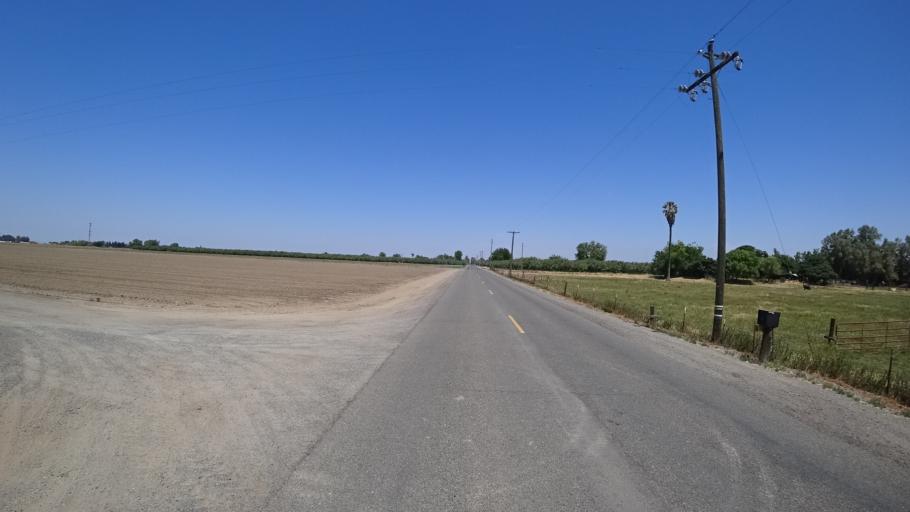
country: US
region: California
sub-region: Kings County
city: Lemoore
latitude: 36.2608
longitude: -119.7630
